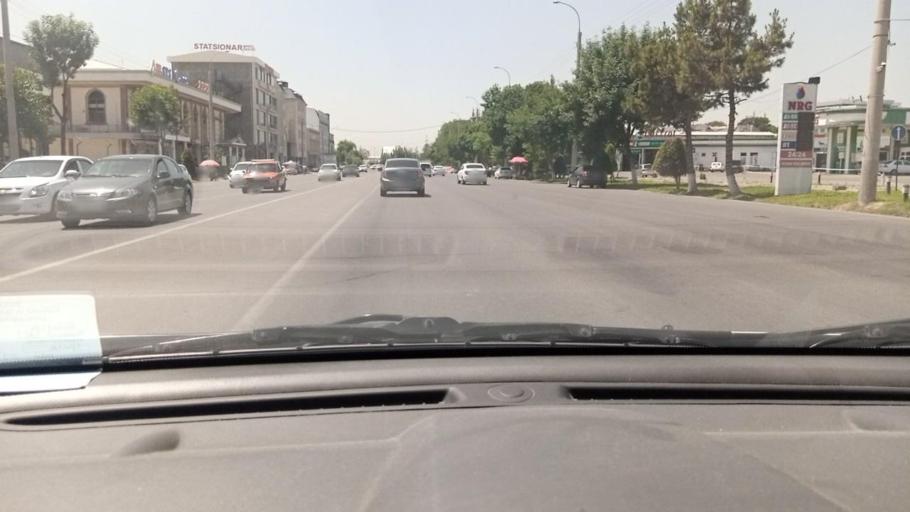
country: UZ
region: Toshkent Shahri
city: Tashkent
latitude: 41.2634
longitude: 69.2341
